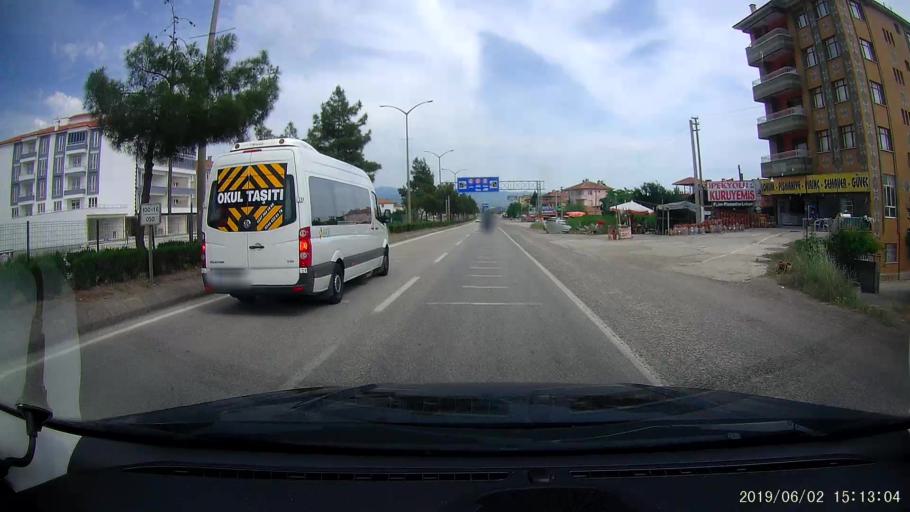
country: TR
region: Corum
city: Osmancik
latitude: 40.9739
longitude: 34.8175
